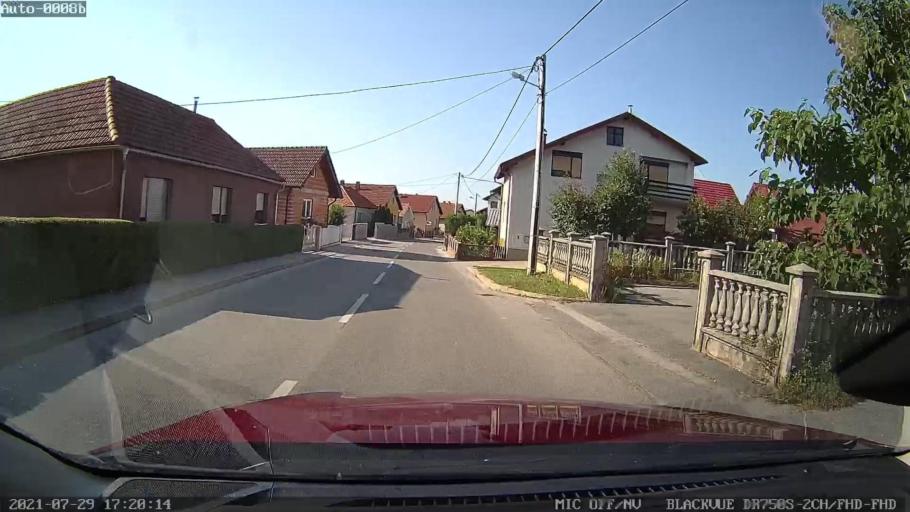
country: HR
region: Varazdinska
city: Ivanec
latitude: 46.2193
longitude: 16.1247
